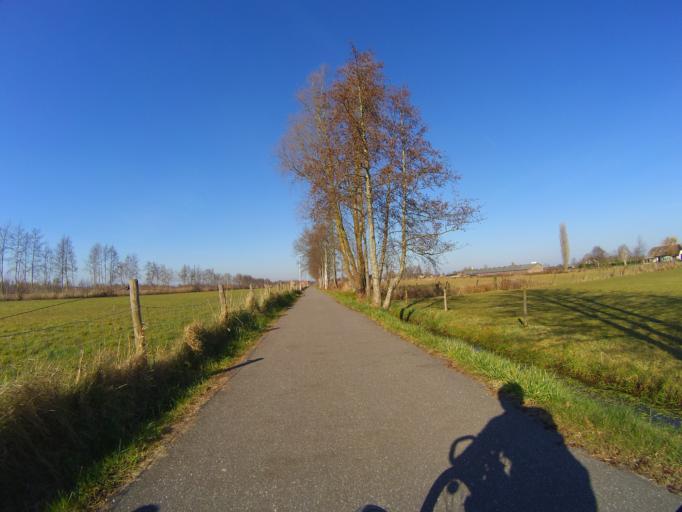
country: NL
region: Gelderland
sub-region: Gemeente Barneveld
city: Zwartebroek
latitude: 52.1824
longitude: 5.4617
